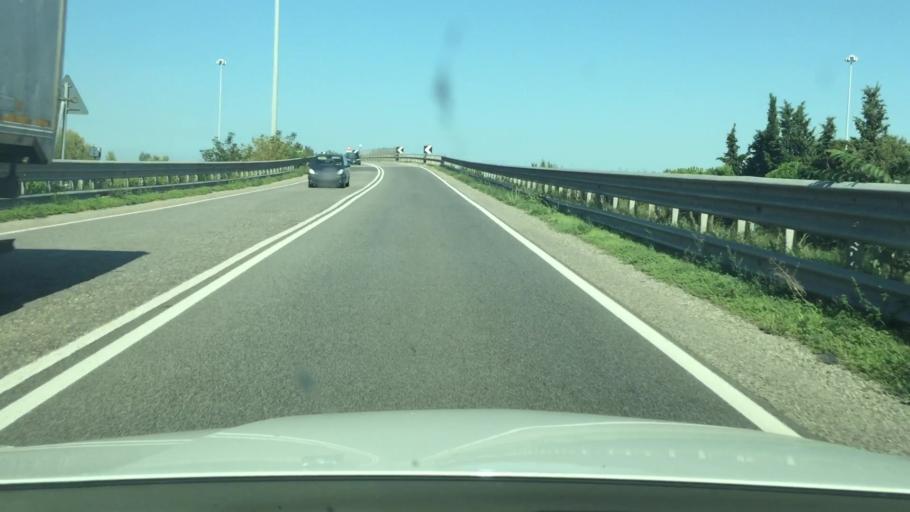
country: IT
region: Emilia-Romagna
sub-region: Provincia di Ravenna
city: Ravenna
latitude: 44.4561
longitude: 12.2067
